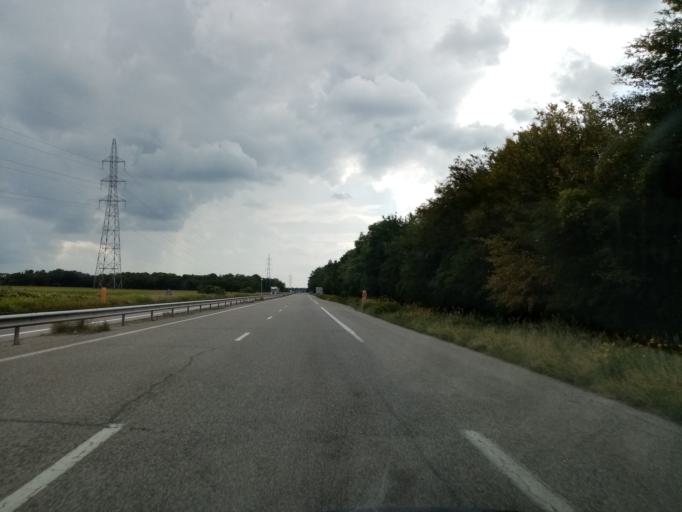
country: FR
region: Alsace
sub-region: Departement du Bas-Rhin
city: Soufflenheim
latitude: 48.8186
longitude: 7.9938
